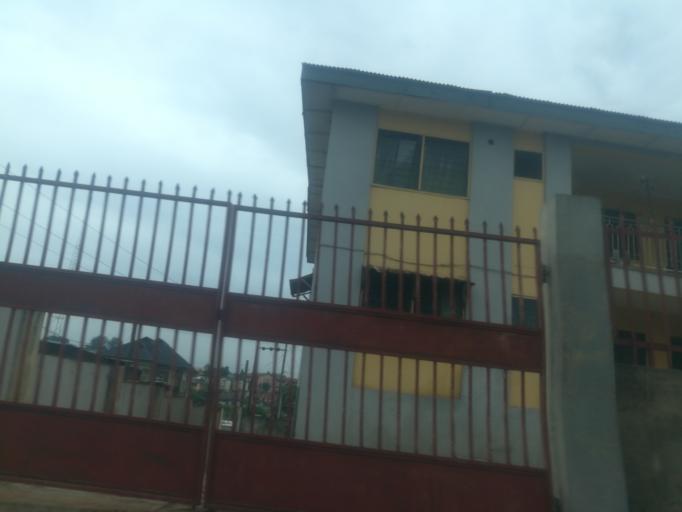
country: NG
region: Oyo
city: Ibadan
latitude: 7.3928
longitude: 3.9373
